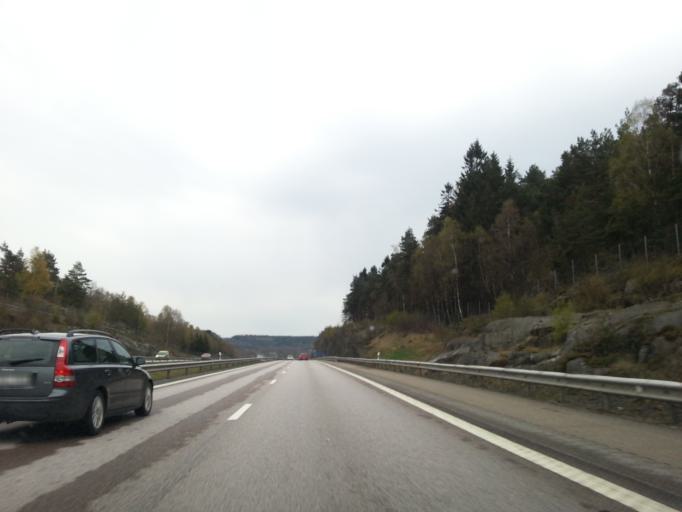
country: SE
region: Halland
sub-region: Kungsbacka Kommun
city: Frillesas
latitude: 57.3345
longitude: 12.2060
